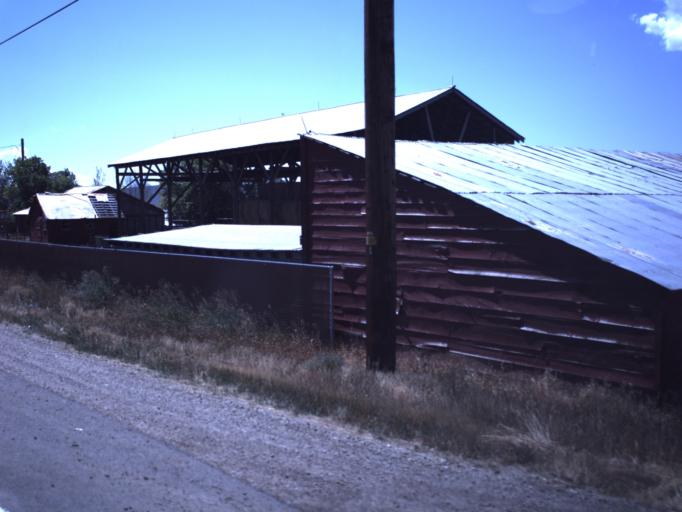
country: US
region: Utah
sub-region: Summit County
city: Oakley
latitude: 40.6883
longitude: -111.2810
